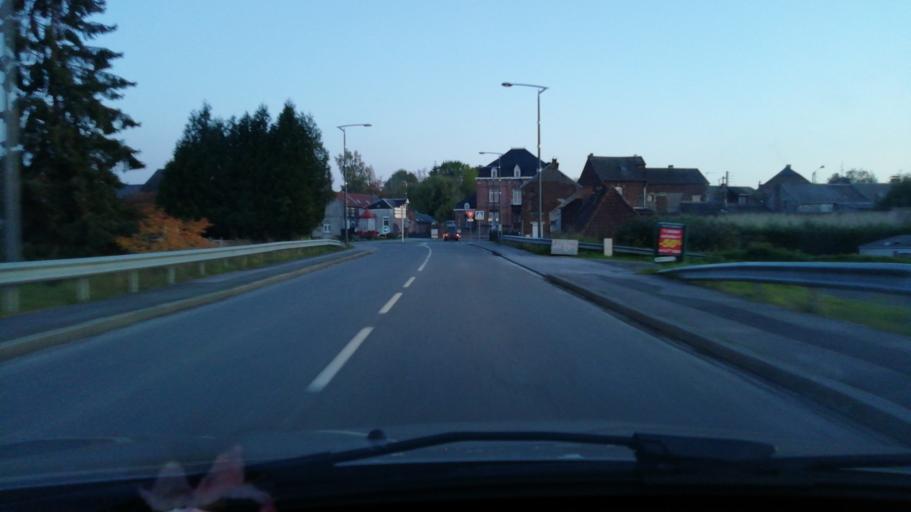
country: FR
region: Nord-Pas-de-Calais
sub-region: Departement du Nord
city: Marpent
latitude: 50.2921
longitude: 4.0787
